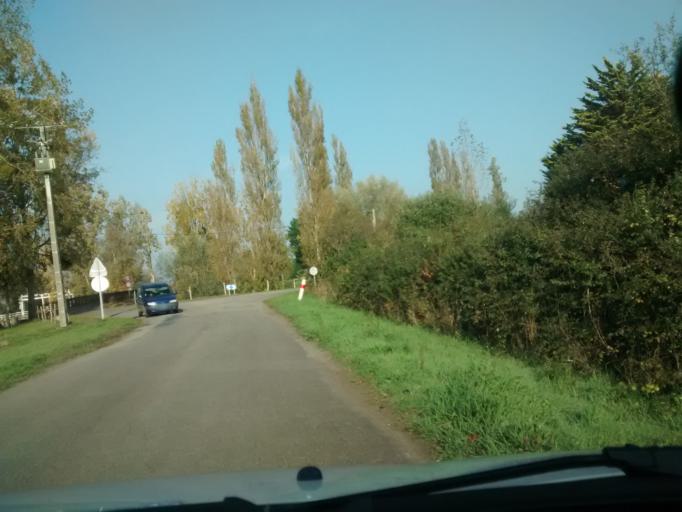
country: FR
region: Pays de la Loire
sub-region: Departement de la Loire-Atlantique
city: Vue
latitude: 47.2378
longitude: -1.8693
